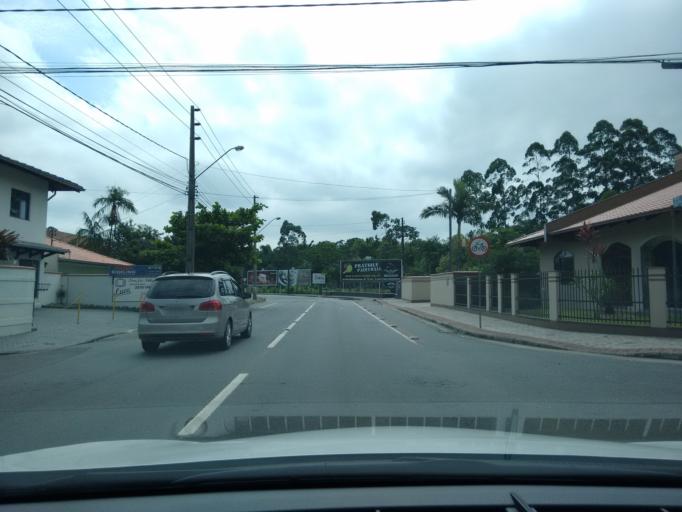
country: BR
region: Santa Catarina
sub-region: Jaragua Do Sul
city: Jaragua do Sul
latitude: -26.4891
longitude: -49.0650
